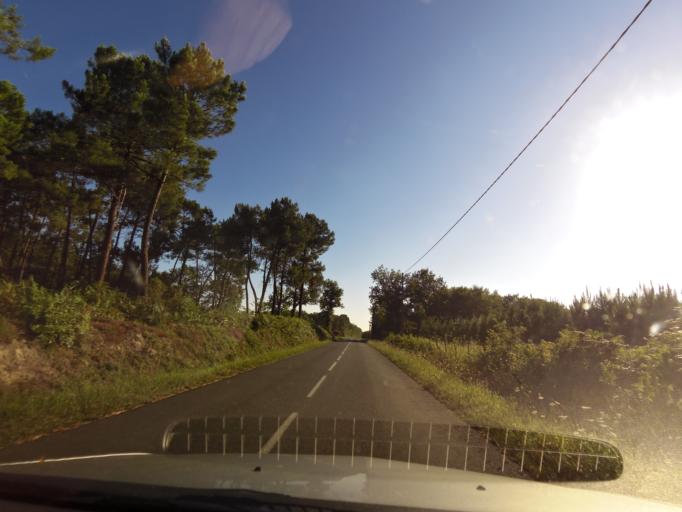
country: FR
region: Aquitaine
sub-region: Departement de la Gironde
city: Castets-en-Dorthe
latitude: 44.5119
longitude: -0.1266
